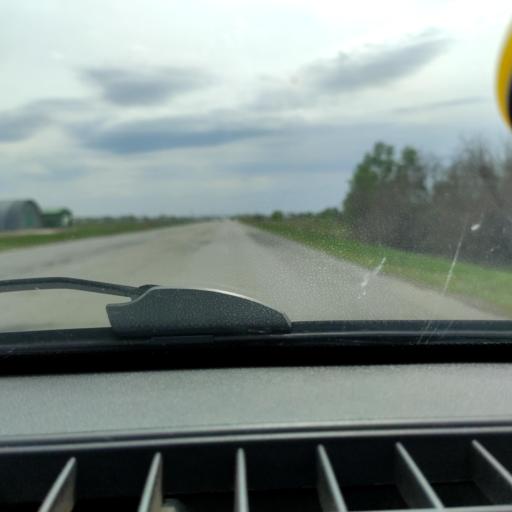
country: RU
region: Samara
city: Tol'yatti
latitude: 53.6841
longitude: 49.4167
